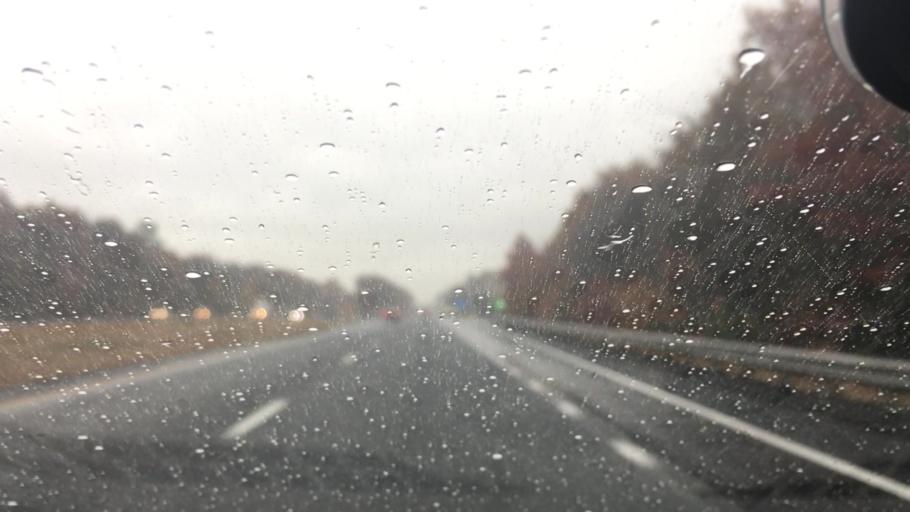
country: US
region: Massachusetts
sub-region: Franklin County
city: Whately
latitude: 42.4503
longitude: -72.6185
